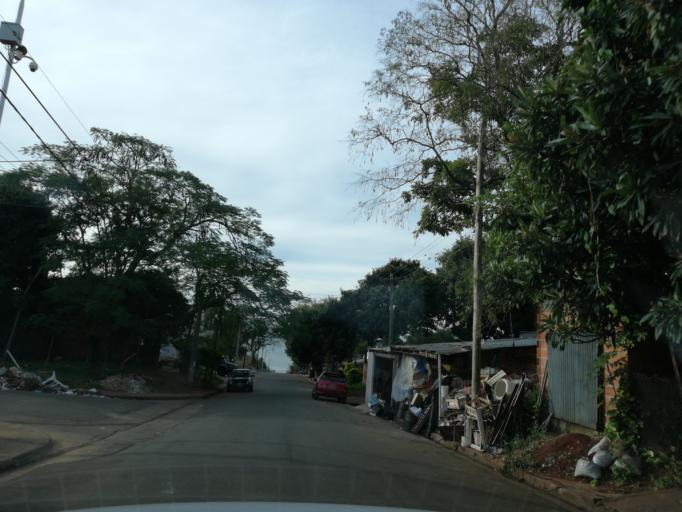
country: AR
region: Misiones
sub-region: Departamento de Capital
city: Posadas
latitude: -27.3570
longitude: -55.9190
